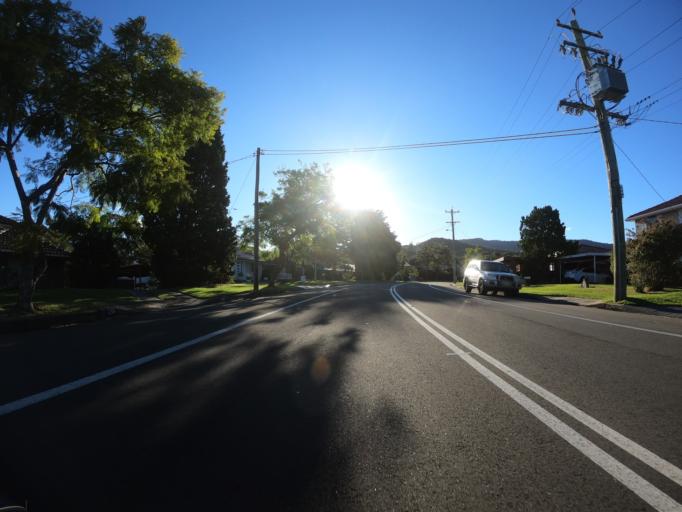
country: AU
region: New South Wales
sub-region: Wollongong
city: Mount Keira
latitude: -34.4310
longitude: 150.8483
